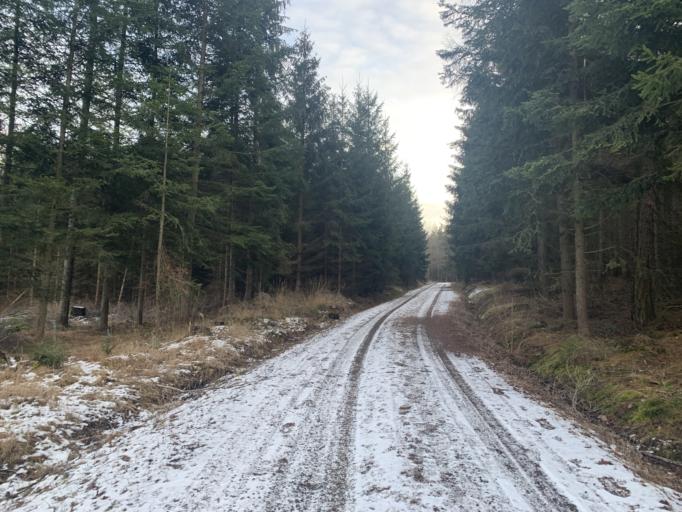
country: CZ
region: Plzensky
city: Zbiroh
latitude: 49.8206
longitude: 13.8011
